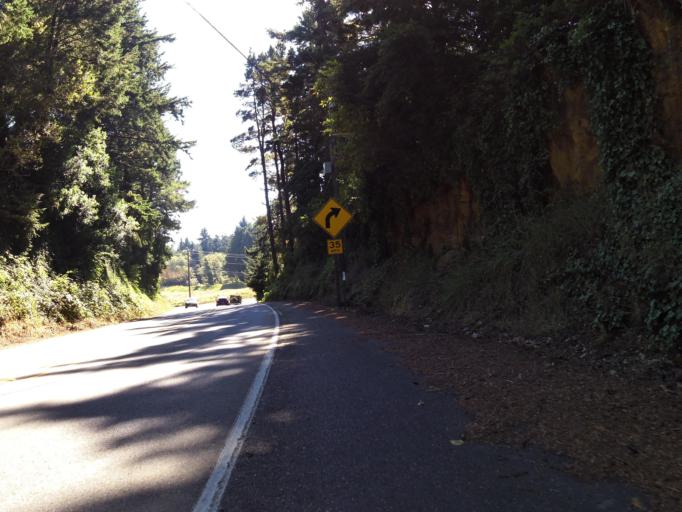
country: US
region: Oregon
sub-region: Coos County
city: Barview
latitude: 43.3459
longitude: -124.3151
